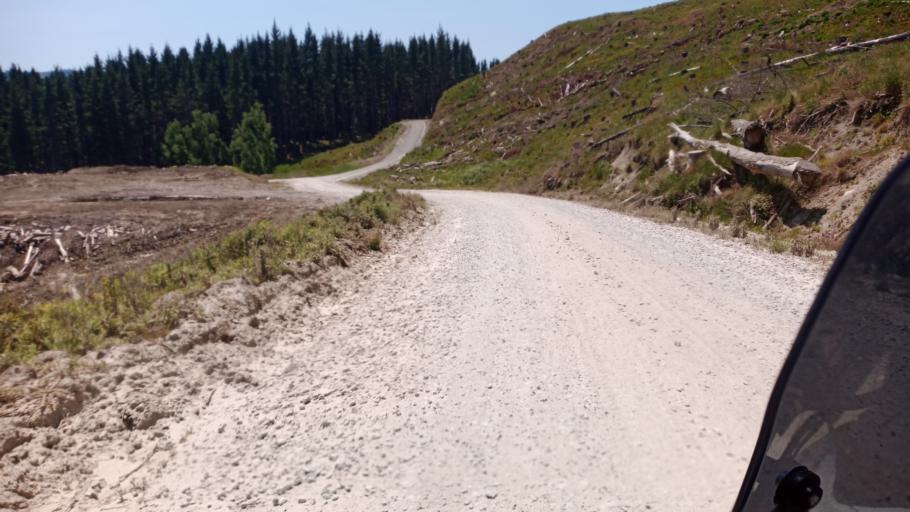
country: NZ
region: Gisborne
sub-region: Gisborne District
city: Gisborne
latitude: -38.2882
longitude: 178.0089
